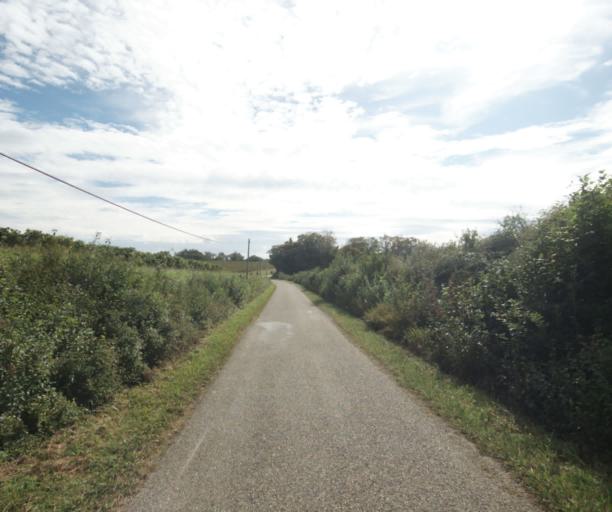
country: FR
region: Aquitaine
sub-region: Departement des Landes
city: Villeneuve-de-Marsan
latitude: 43.9010
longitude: -0.1946
